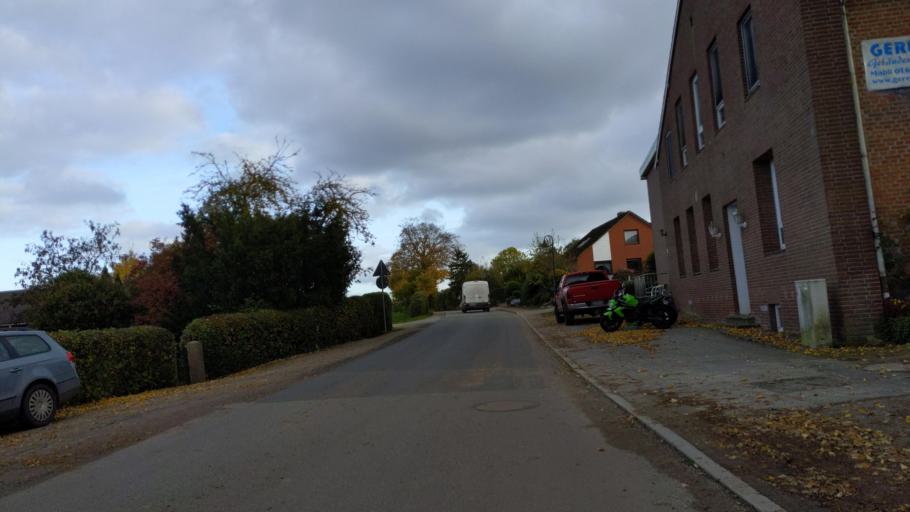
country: DE
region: Schleswig-Holstein
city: Susel
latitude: 54.1050
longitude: 10.7160
